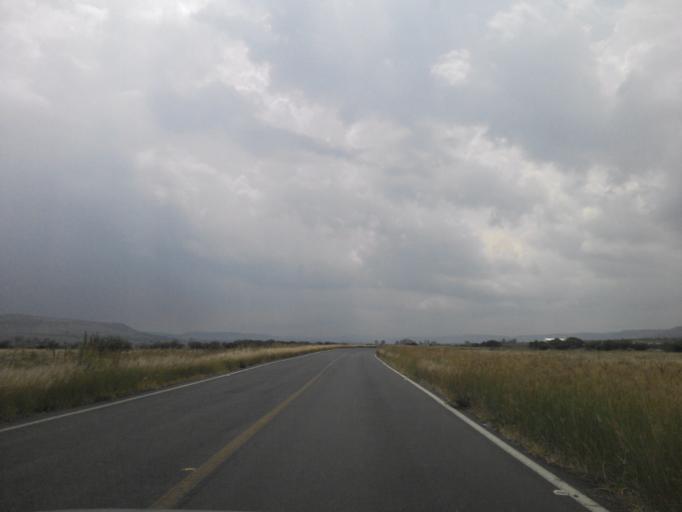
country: MX
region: Jalisco
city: San Diego de Alejandria
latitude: 20.8978
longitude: -102.0080
